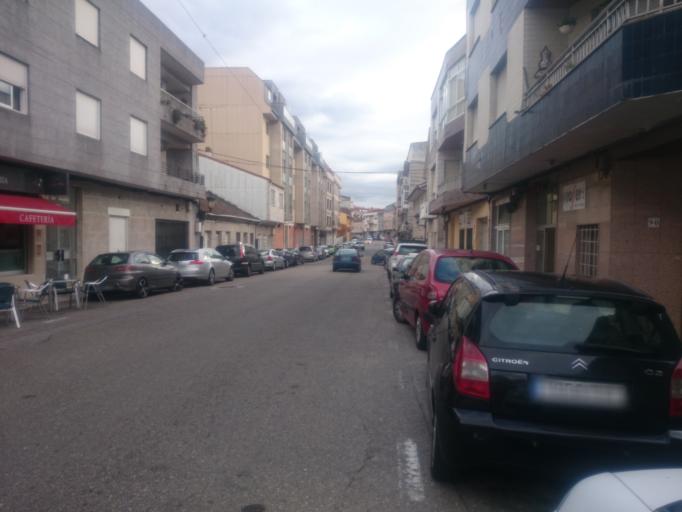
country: ES
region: Galicia
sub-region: Provincia de Pontevedra
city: Porrino
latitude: 42.1571
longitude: -8.6203
